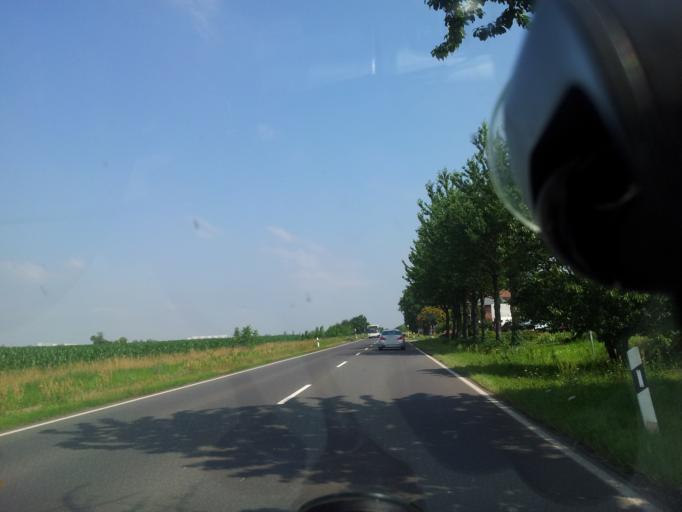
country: DE
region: Saxony-Anhalt
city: Magdeburg
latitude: 52.0672
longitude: 11.6150
